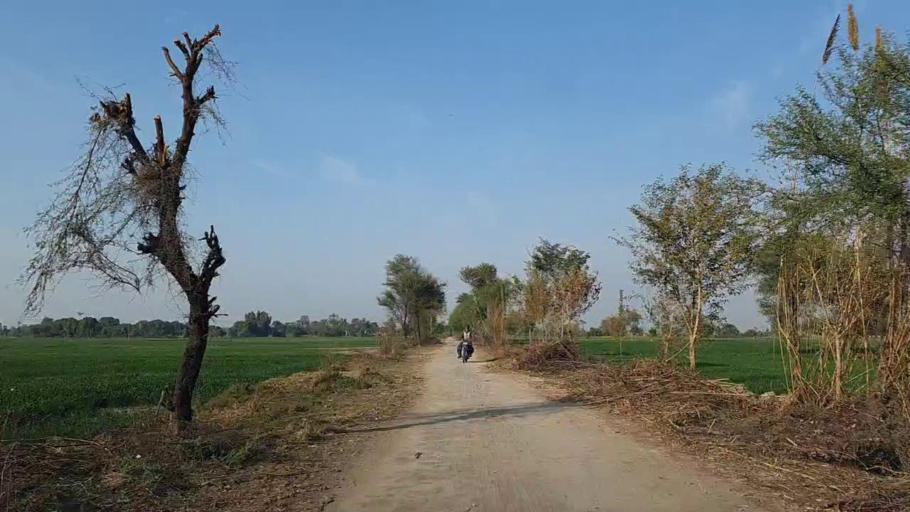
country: PK
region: Sindh
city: Nawabshah
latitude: 26.3776
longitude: 68.4850
